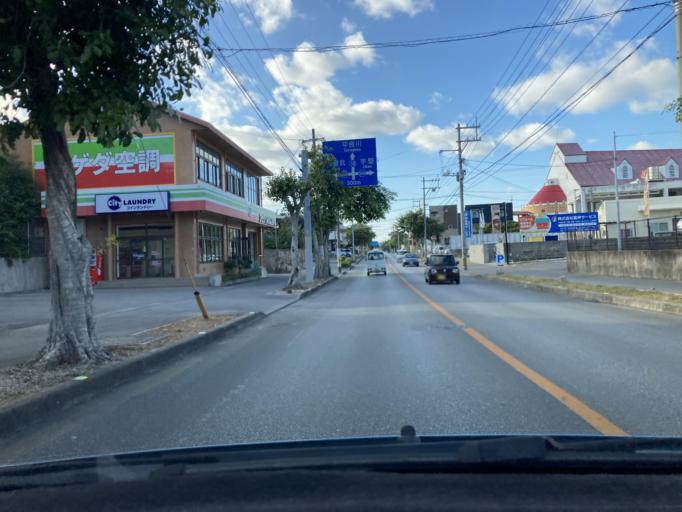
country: JP
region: Okinawa
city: Gushikawa
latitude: 26.3635
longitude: 127.8573
